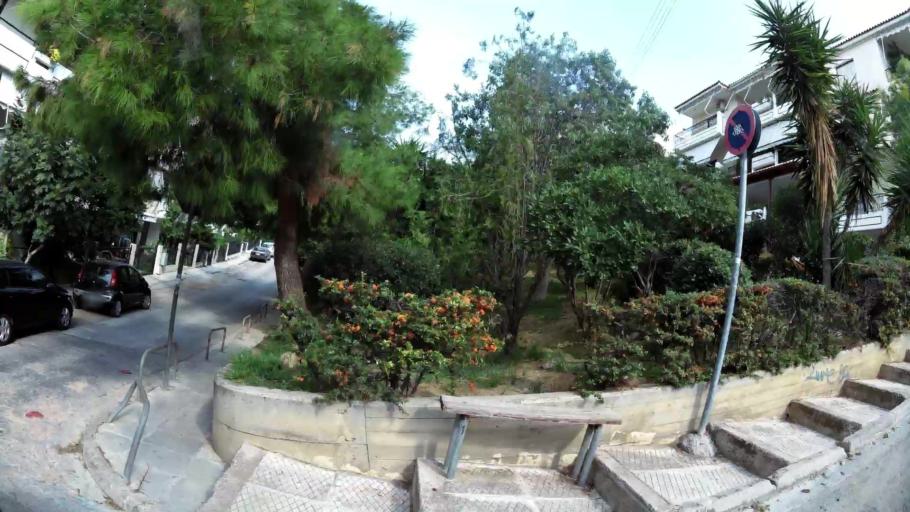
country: GR
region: Attica
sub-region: Nomarchia Athinas
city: Galatsi
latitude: 38.0111
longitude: 23.7594
